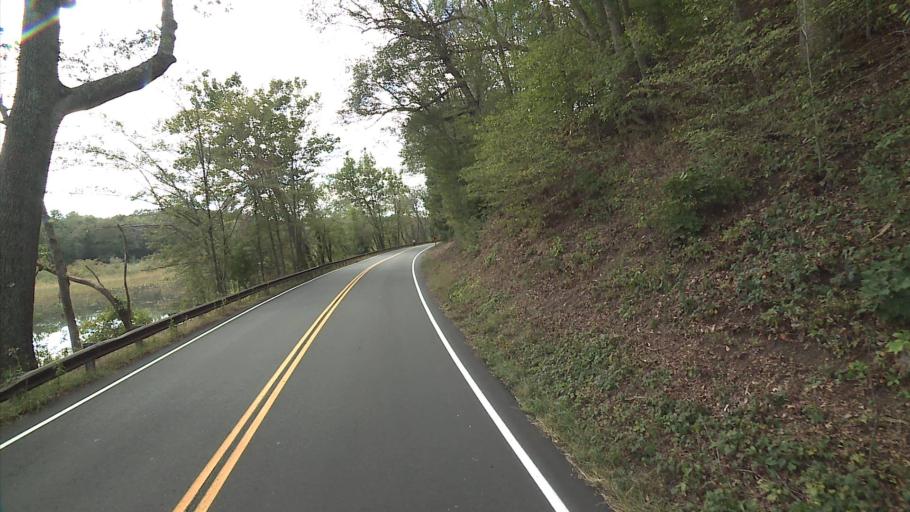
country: US
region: Connecticut
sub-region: Middlesex County
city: Chester Center
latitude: 41.4092
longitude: -72.4440
